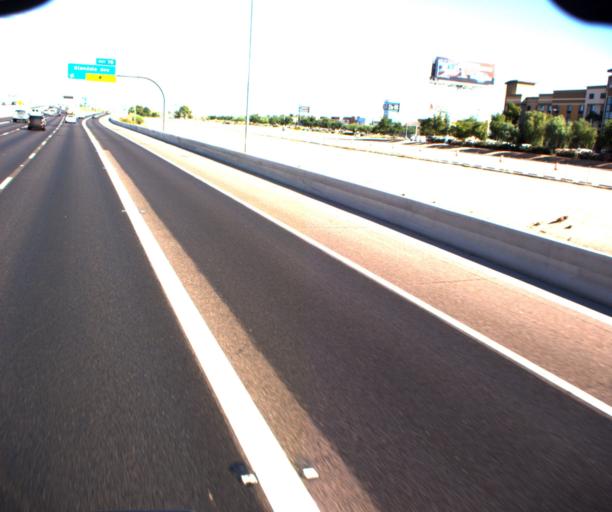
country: US
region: Arizona
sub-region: Maricopa County
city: Peoria
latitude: 33.5303
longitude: -112.2689
